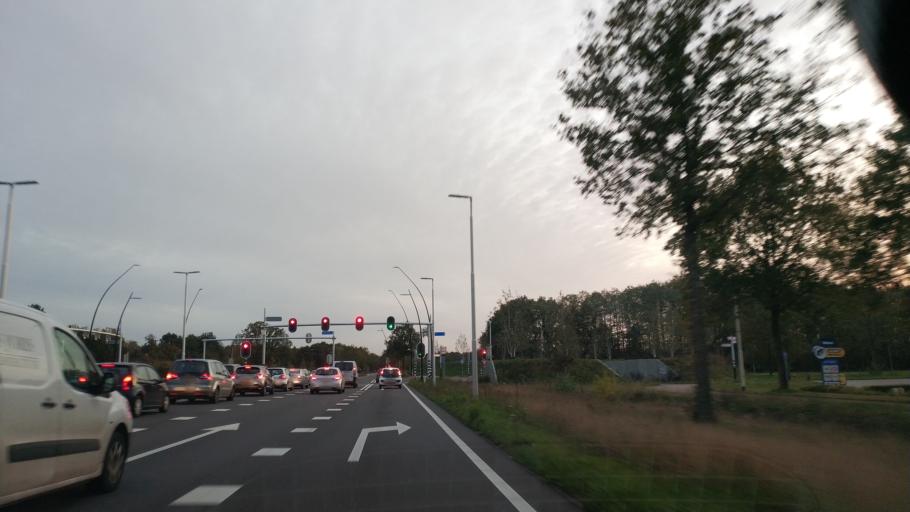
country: NL
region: North Brabant
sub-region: Gemeente Goirle
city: Goirle
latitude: 51.5314
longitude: 5.0445
